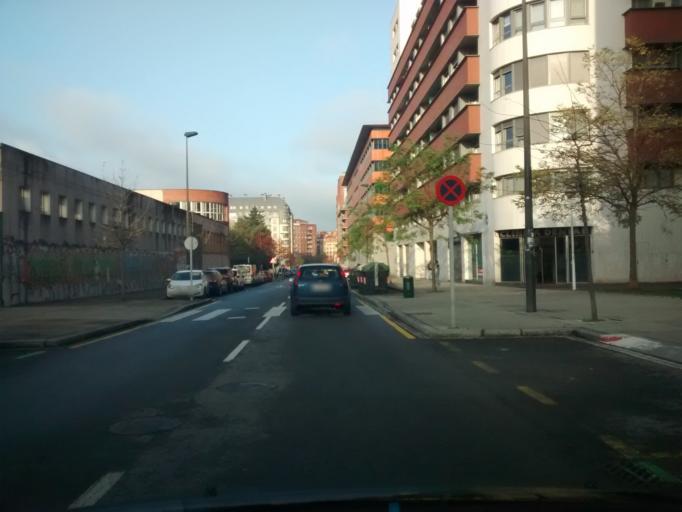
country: ES
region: Basque Country
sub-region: Bizkaia
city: Santutxu
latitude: 43.2491
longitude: -2.9294
